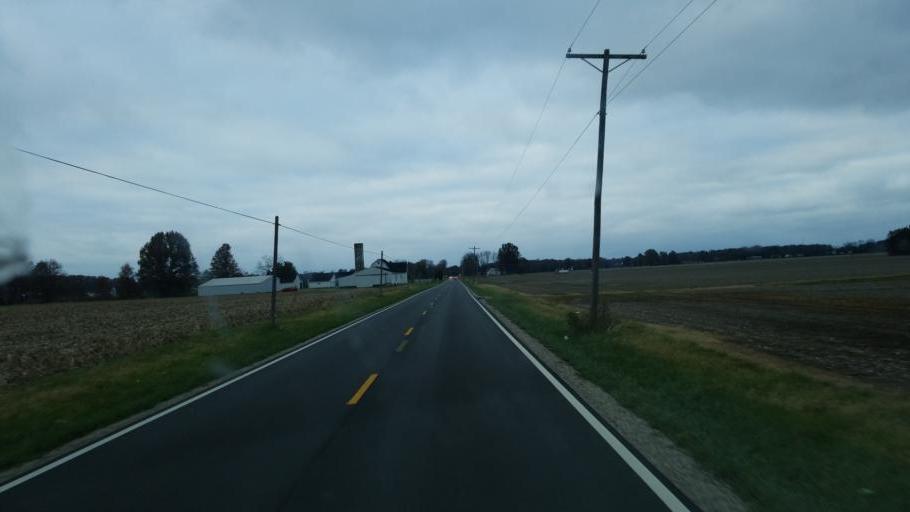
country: US
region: Ohio
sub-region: Delaware County
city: Ashley
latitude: 40.3222
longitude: -82.9156
